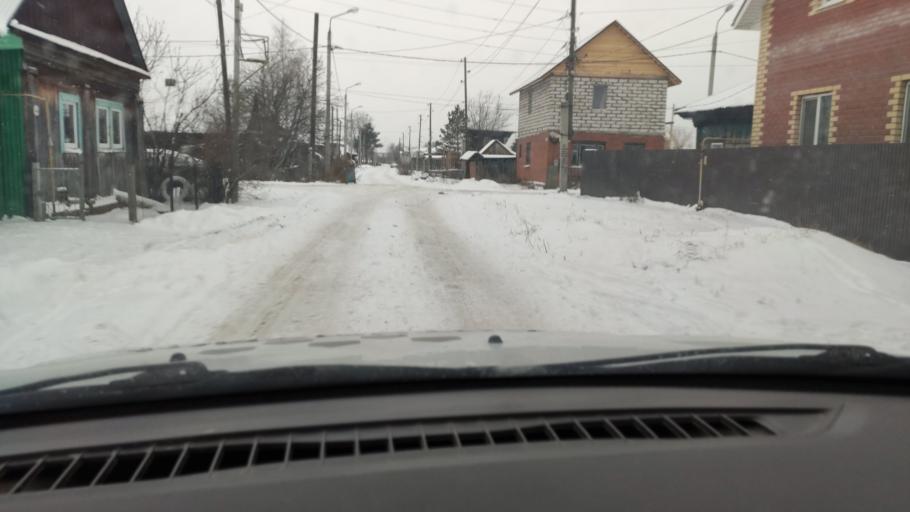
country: RU
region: Perm
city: Kondratovo
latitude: 57.9609
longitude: 56.1225
